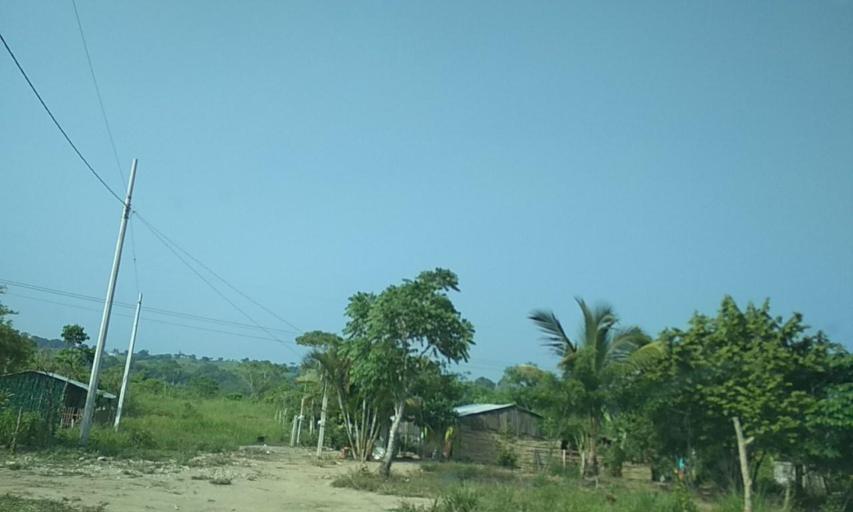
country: MX
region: Veracruz
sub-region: Atzalan
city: Colonias Pedernales
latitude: 20.0508
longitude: -96.9928
